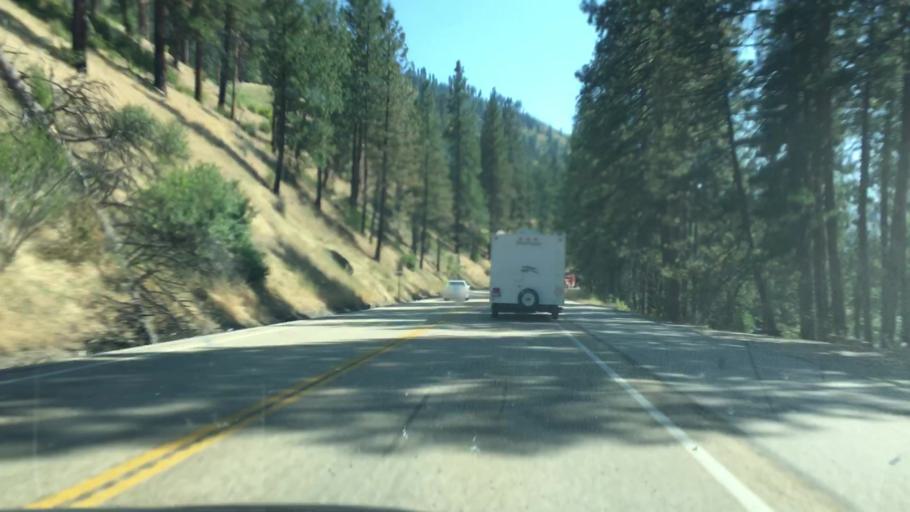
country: US
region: Idaho
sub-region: Boise County
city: Idaho City
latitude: 44.0711
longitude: -116.1186
